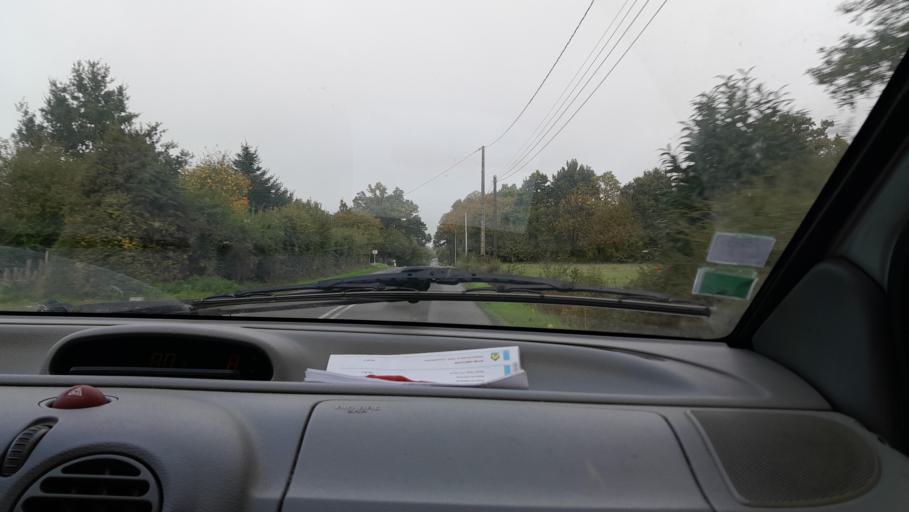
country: FR
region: Brittany
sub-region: Departement d'Ille-et-Vilaine
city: Luitre
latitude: 48.2326
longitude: -1.1050
